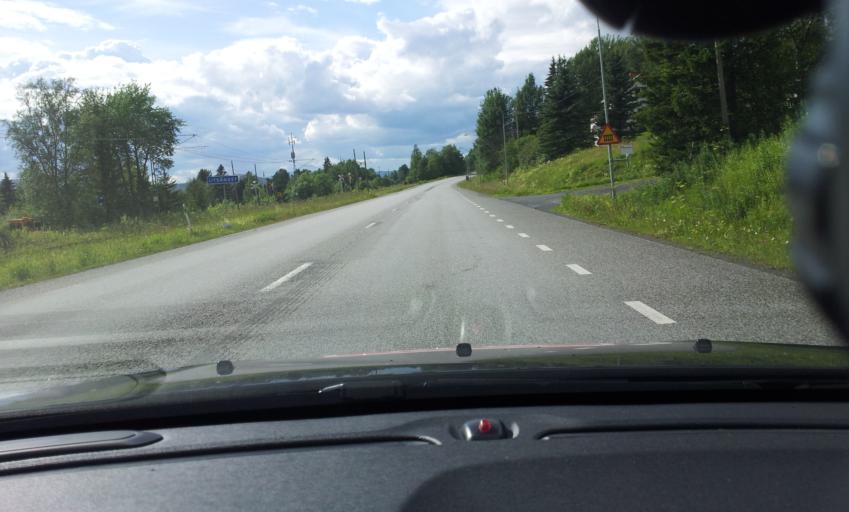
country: SE
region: Jaemtland
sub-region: Are Kommun
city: Jarpen
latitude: 63.3099
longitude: 13.6126
